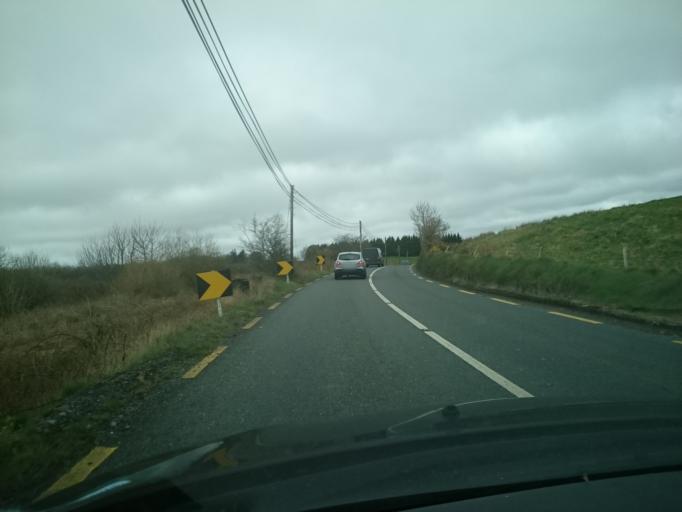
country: IE
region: Connaught
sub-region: Maigh Eo
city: Kiltamagh
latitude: 53.7905
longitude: -9.0900
